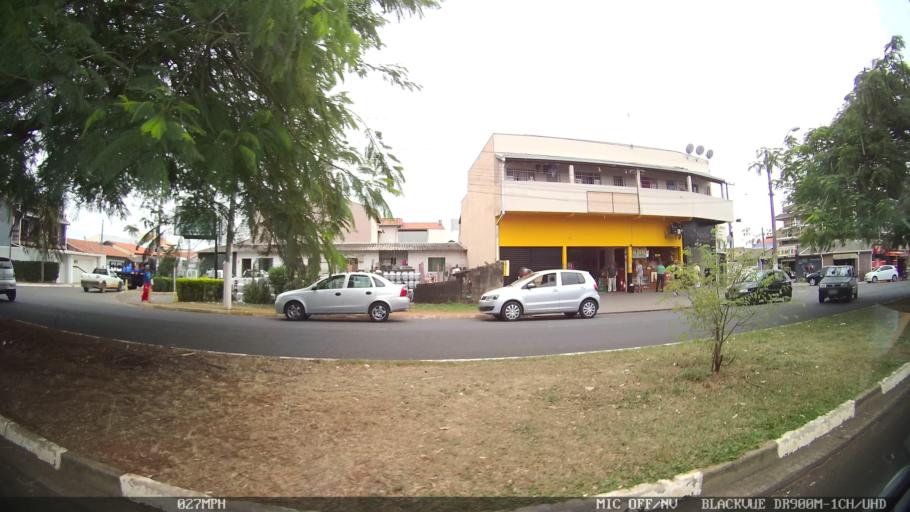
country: BR
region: Sao Paulo
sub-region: Paulinia
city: Paulinia
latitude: -22.7177
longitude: -47.1723
